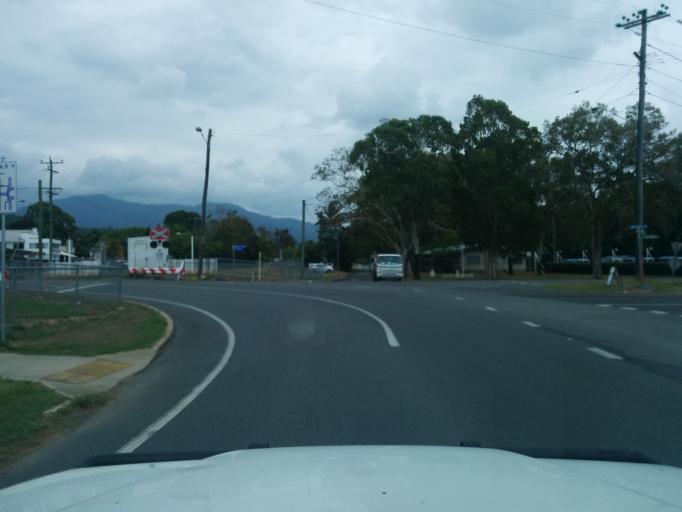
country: AU
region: Queensland
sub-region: Cairns
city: Redlynch
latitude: -16.8748
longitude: 145.7346
